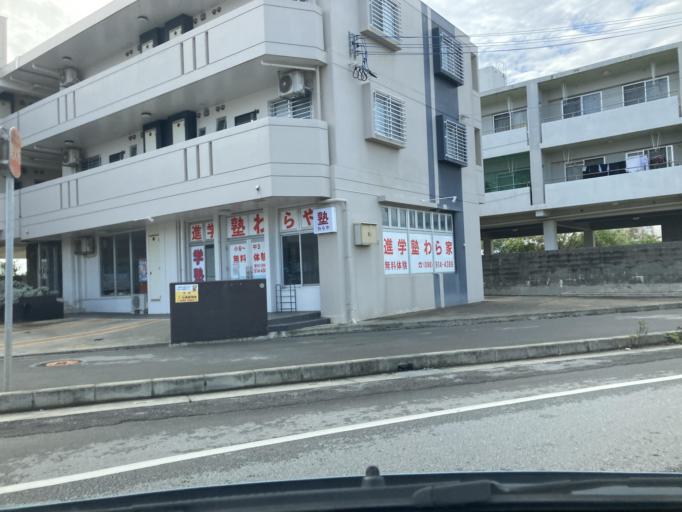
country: JP
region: Okinawa
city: Tomigusuku
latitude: 26.1504
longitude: 127.7236
